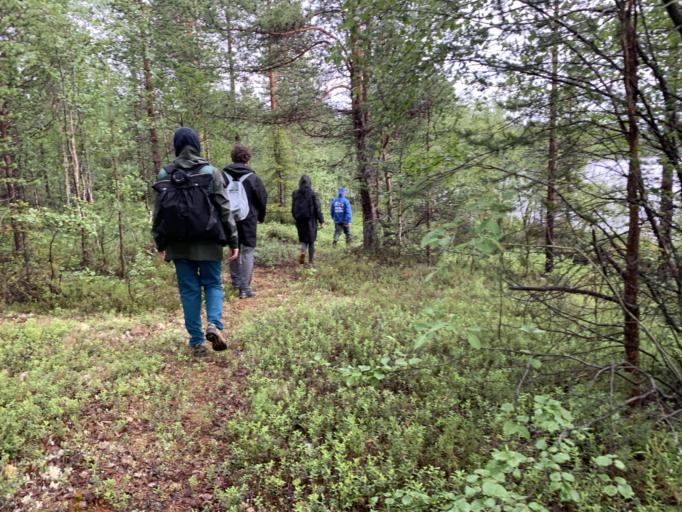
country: RU
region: Murmansk
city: Monchegorsk
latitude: 67.9396
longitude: 33.0388
